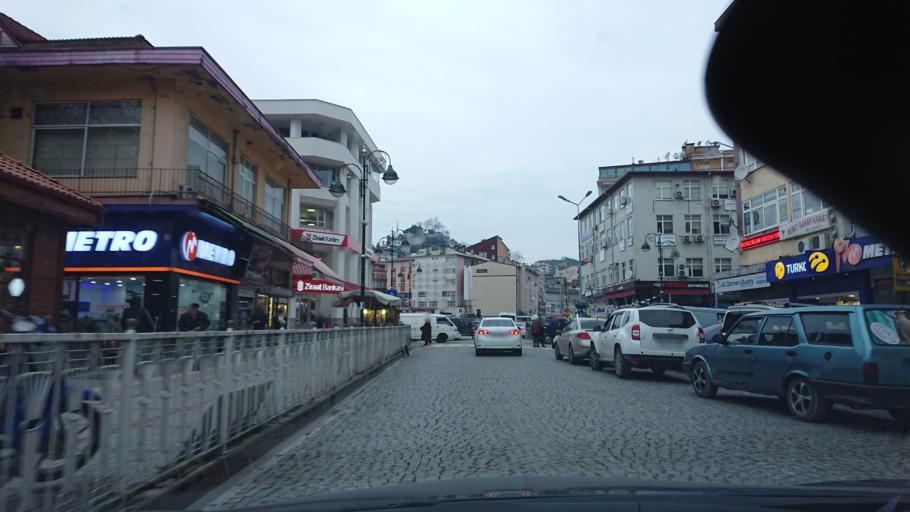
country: TR
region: Rize
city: Rize
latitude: 41.0254
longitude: 40.5181
